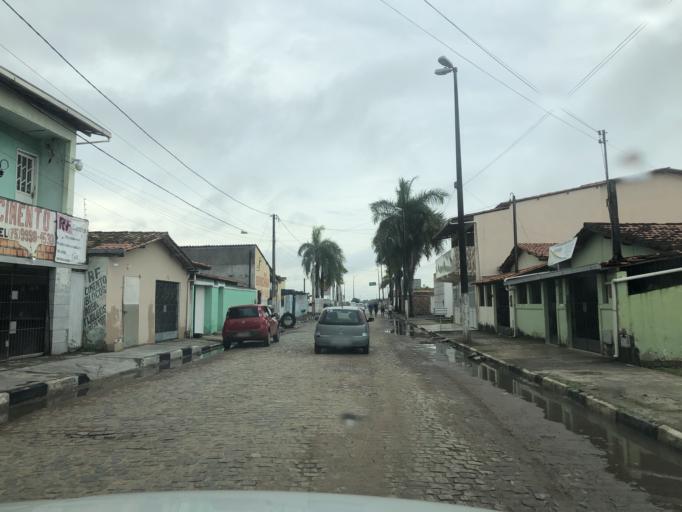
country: BR
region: Bahia
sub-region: Esplanada
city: Esplanada
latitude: -11.7954
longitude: -37.9538
